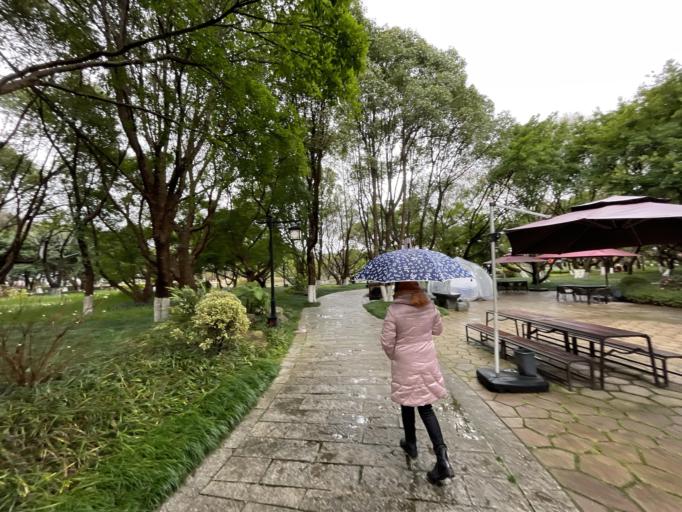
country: CN
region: Zhejiang Sheng
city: Oubei
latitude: 28.0323
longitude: 120.6454
